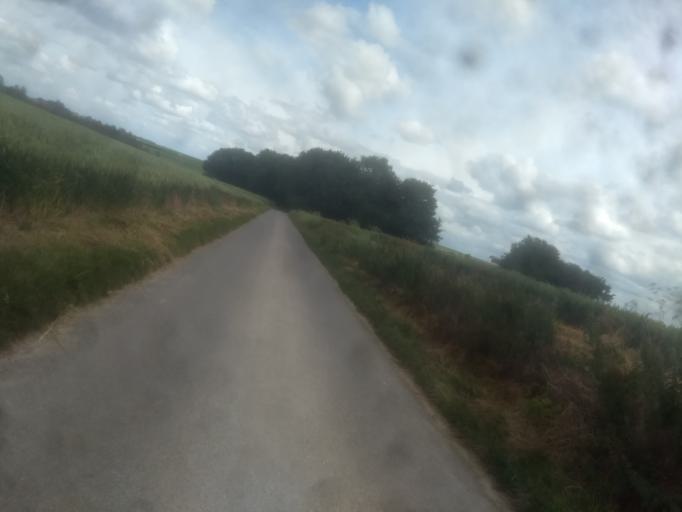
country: FR
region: Nord-Pas-de-Calais
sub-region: Departement du Pas-de-Calais
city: Duisans
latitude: 50.3053
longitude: 2.6704
